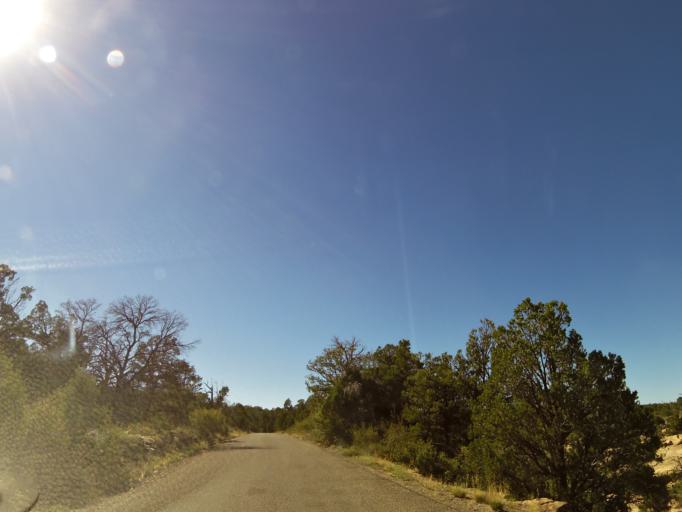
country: US
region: Colorado
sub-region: Montezuma County
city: Cortez
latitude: 37.1650
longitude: -108.4798
